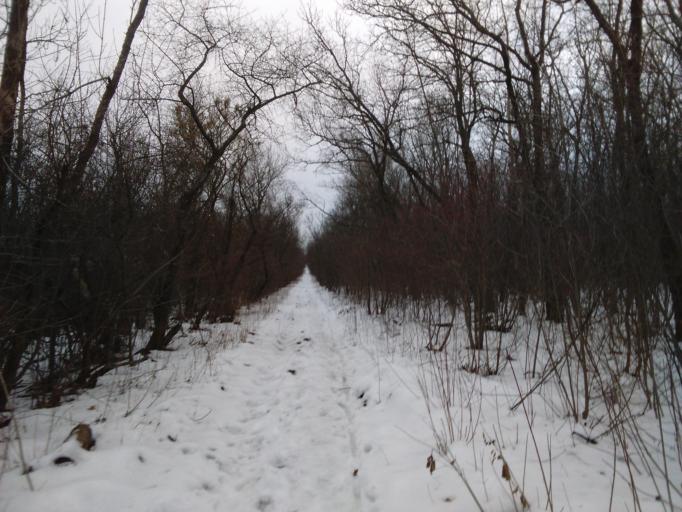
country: RU
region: Rostov
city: Temernik
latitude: 47.3526
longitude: 39.7397
